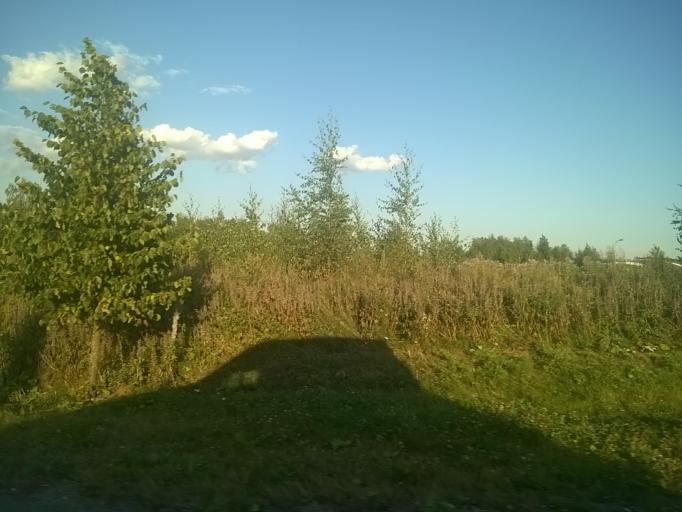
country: FI
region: Pirkanmaa
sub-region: Tampere
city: Tampere
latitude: 61.4670
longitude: 23.7257
